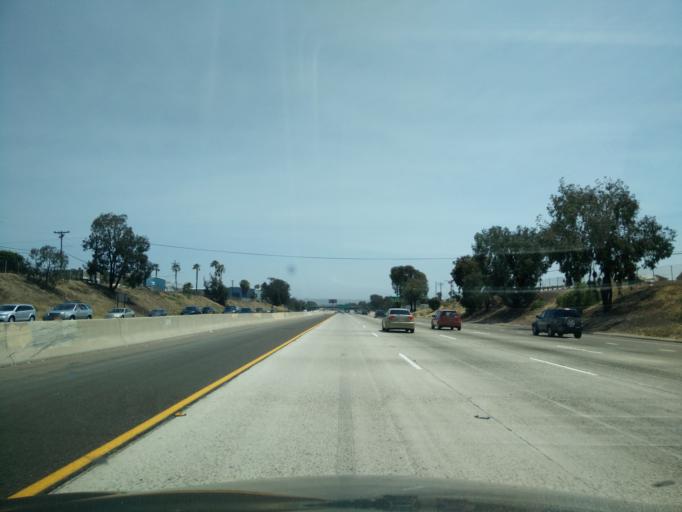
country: US
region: California
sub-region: San Diego County
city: Imperial Beach
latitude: 32.6013
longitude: -117.0897
